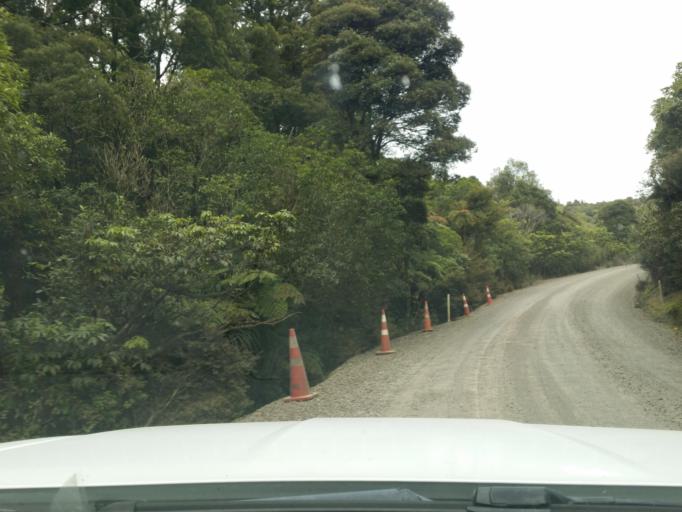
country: NZ
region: Northland
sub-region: Kaipara District
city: Dargaville
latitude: -35.7160
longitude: 173.6401
